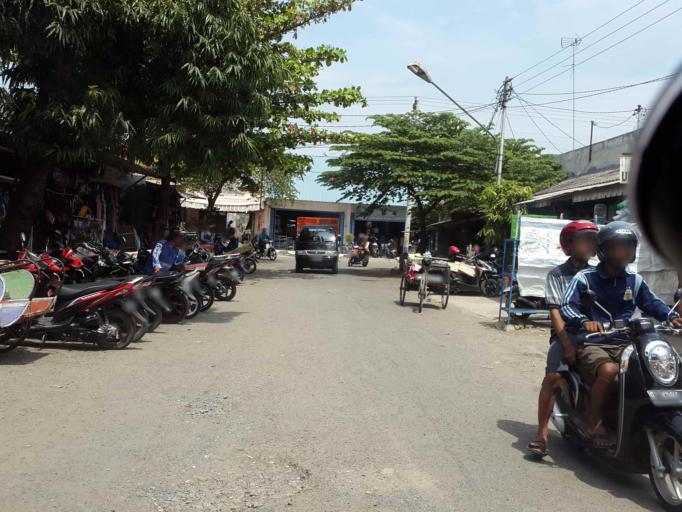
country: ID
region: Central Java
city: Pemalang
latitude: -6.8896
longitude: 109.3909
